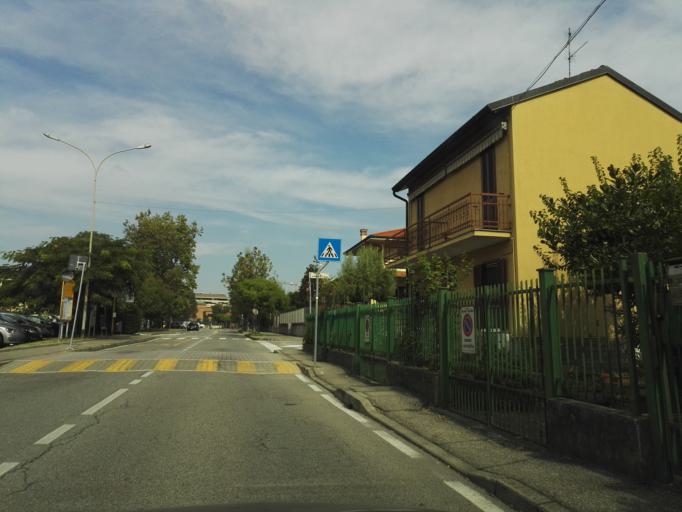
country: IT
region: Lombardy
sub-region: Citta metropolitana di Milano
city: Bettola-Zeloforomagno
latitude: 45.4230
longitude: 9.3089
